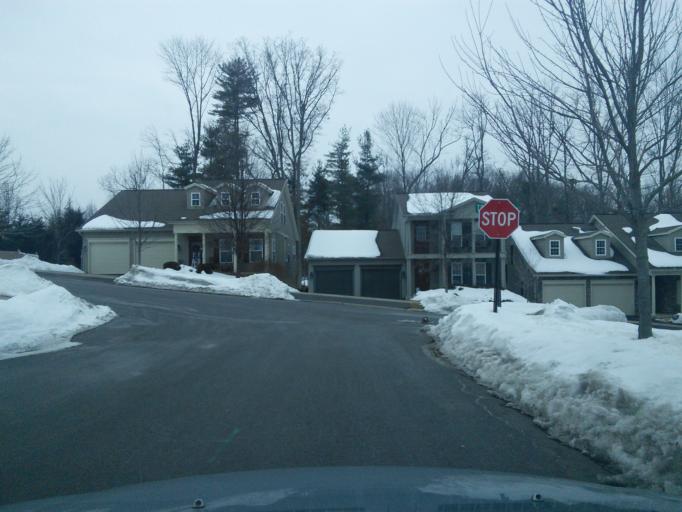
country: US
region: Pennsylvania
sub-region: Centre County
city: State College
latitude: 40.8268
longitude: -77.8786
